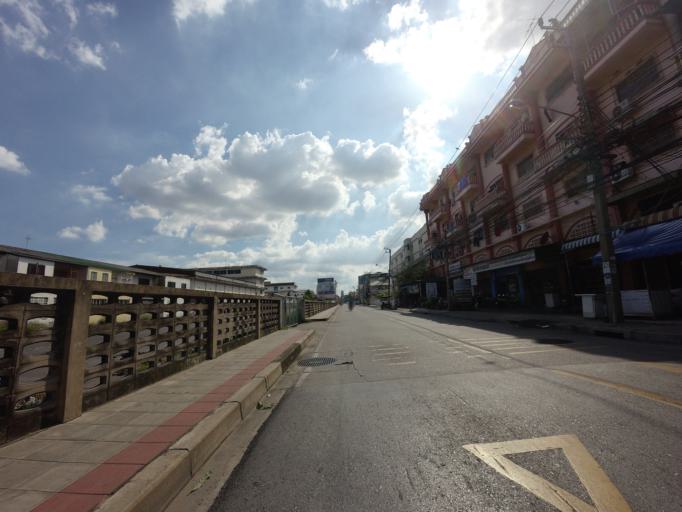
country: TH
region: Bangkok
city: Wang Thonglang
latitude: 13.7822
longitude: 100.5964
